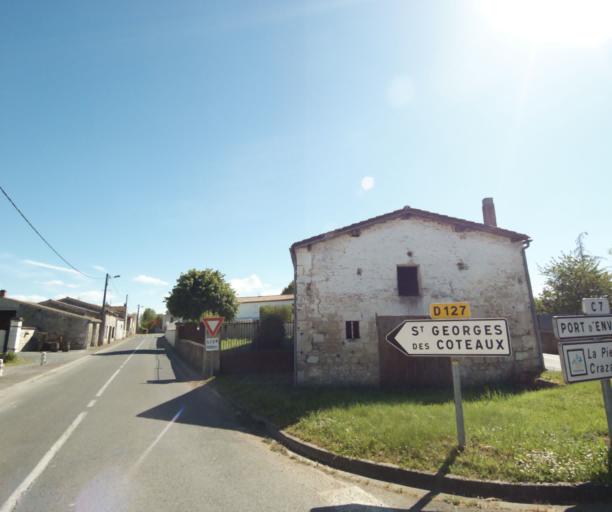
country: FR
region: Poitou-Charentes
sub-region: Departement de la Charente-Maritime
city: Bussac-sur-Charente
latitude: 45.8218
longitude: -0.6588
